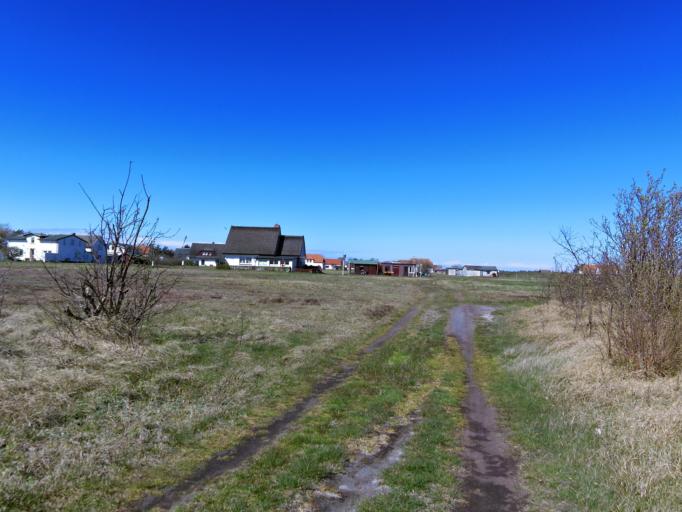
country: DE
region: Mecklenburg-Vorpommern
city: Hiddensee
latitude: 54.5222
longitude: 13.0893
